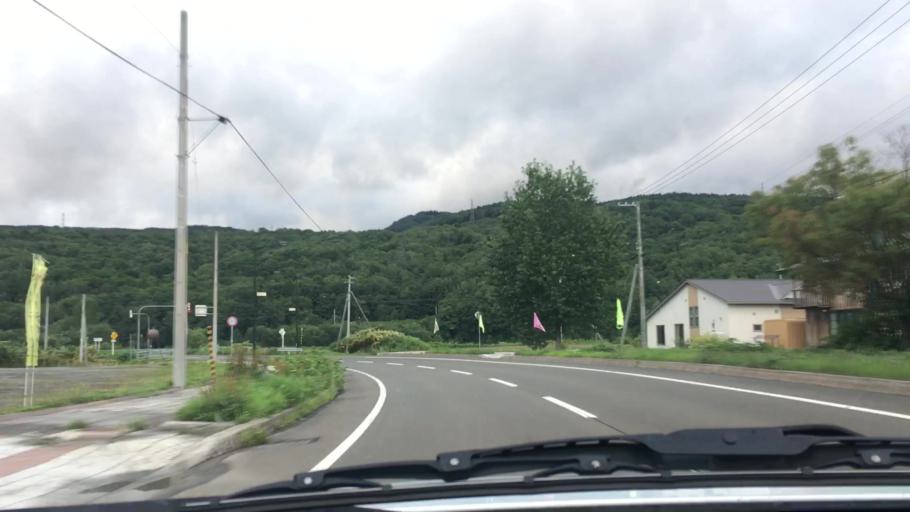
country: JP
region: Hokkaido
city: Shimo-furano
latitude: 42.9805
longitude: 142.3954
